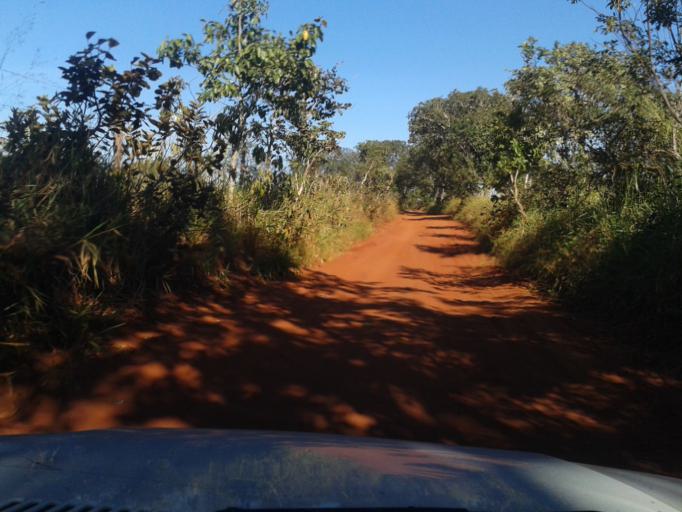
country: BR
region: Minas Gerais
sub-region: Ituiutaba
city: Ituiutaba
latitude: -19.0874
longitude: -49.7785
